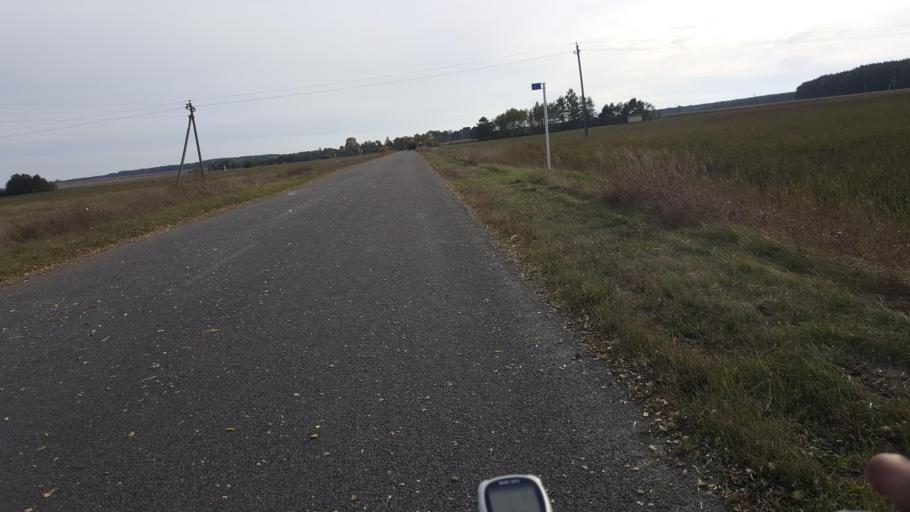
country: BY
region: Brest
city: Kamyanyets
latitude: 52.4022
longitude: 23.8863
